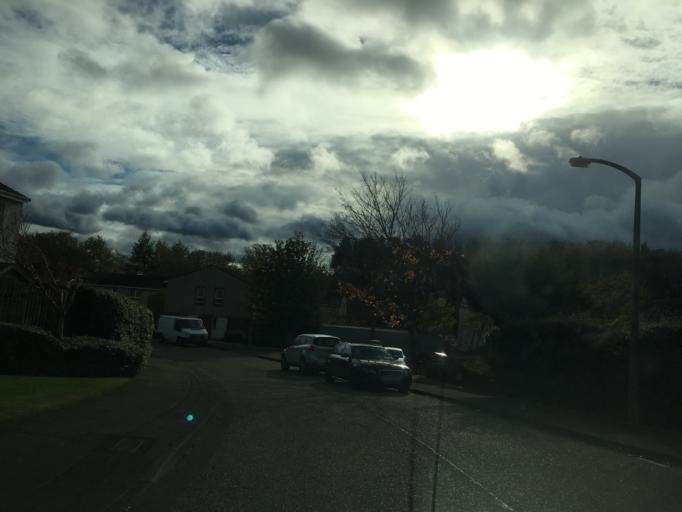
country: GB
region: Scotland
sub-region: Midlothian
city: Loanhead
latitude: 55.9043
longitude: -3.1749
